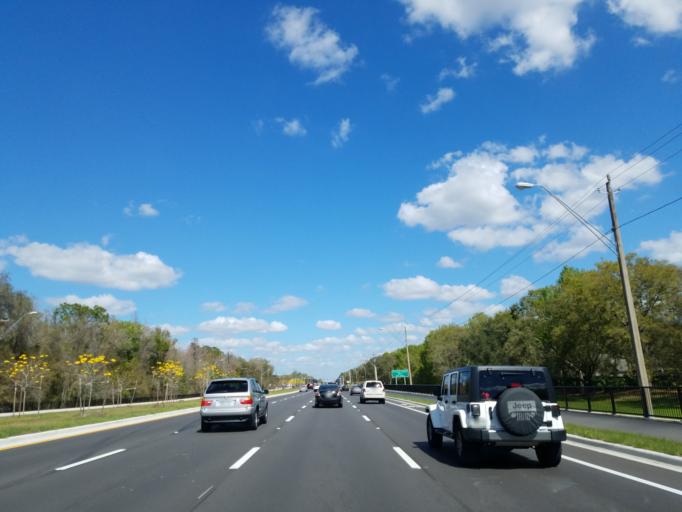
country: US
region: Florida
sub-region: Hillsborough County
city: University
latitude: 28.0945
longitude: -82.4016
